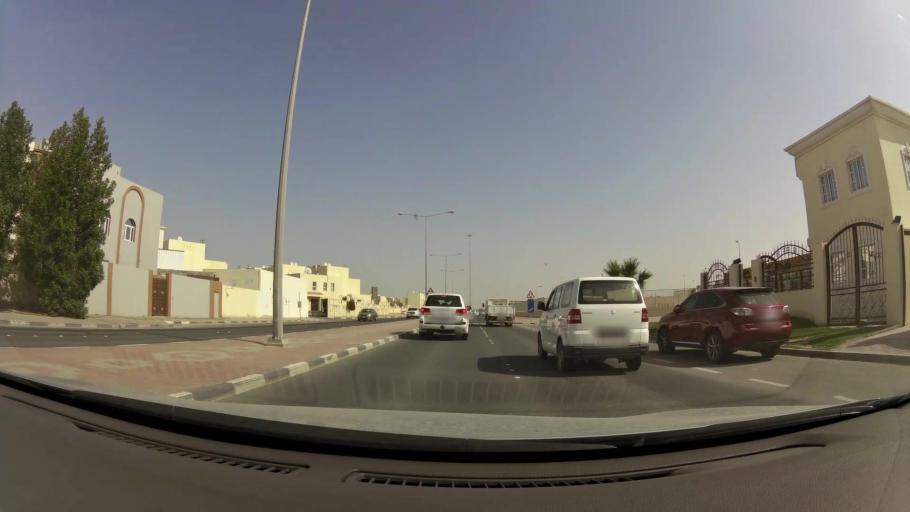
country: QA
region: Baladiyat ar Rayyan
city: Ar Rayyan
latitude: 25.3465
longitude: 51.4453
